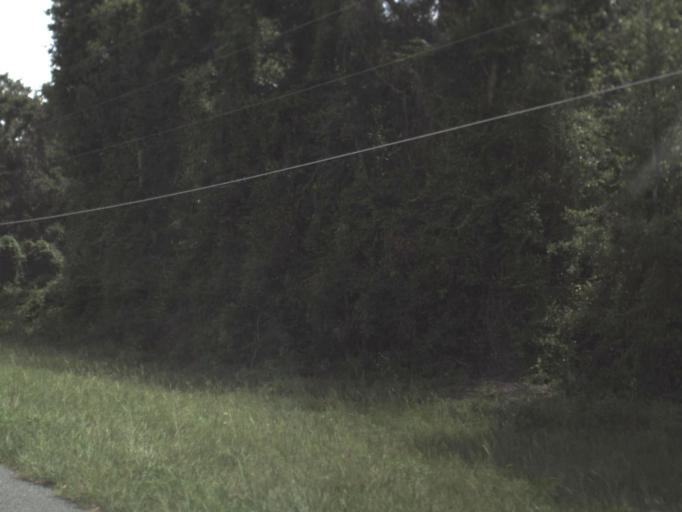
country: US
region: Florida
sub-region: Citrus County
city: Hernando
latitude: 28.9350
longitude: -82.3774
